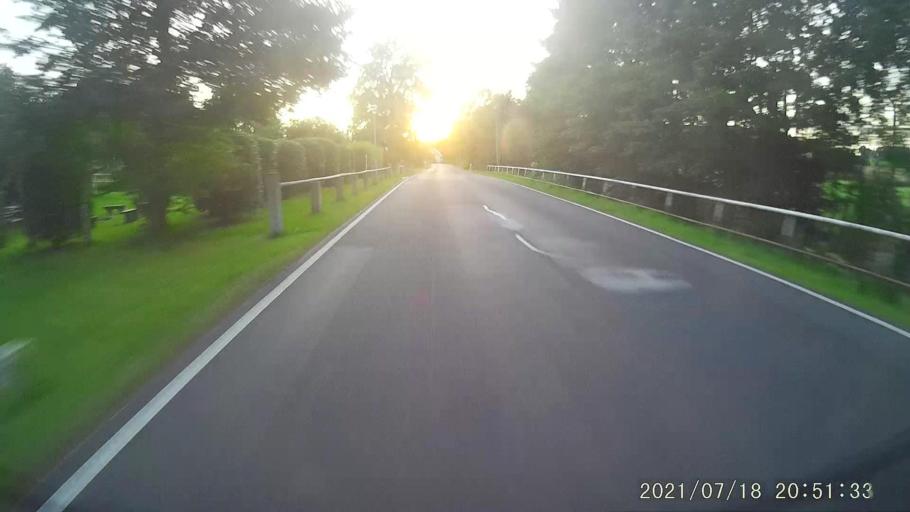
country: DE
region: Saxony
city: Konigshain
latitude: 51.1829
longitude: 14.8553
